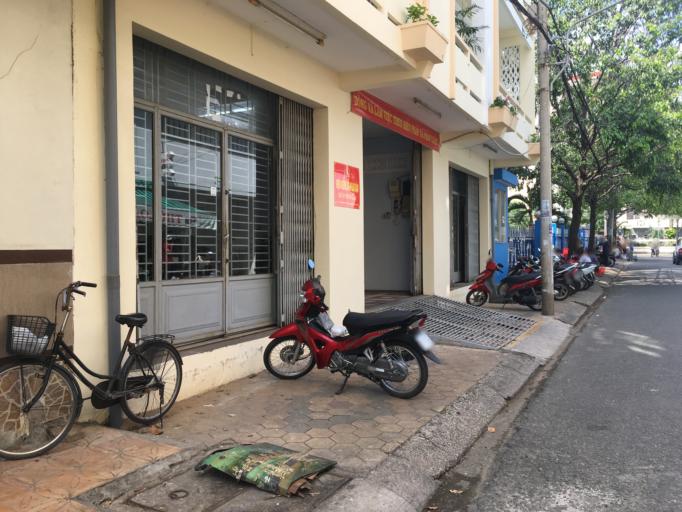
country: VN
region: Can Tho
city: Can Tho
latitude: 10.0346
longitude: 105.7878
